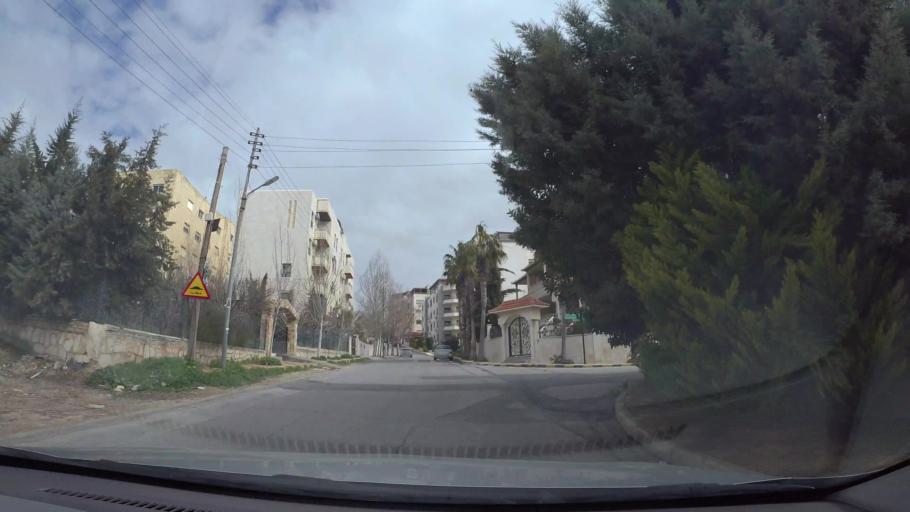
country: JO
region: Amman
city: Al Jubayhah
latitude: 32.0031
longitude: 35.8389
